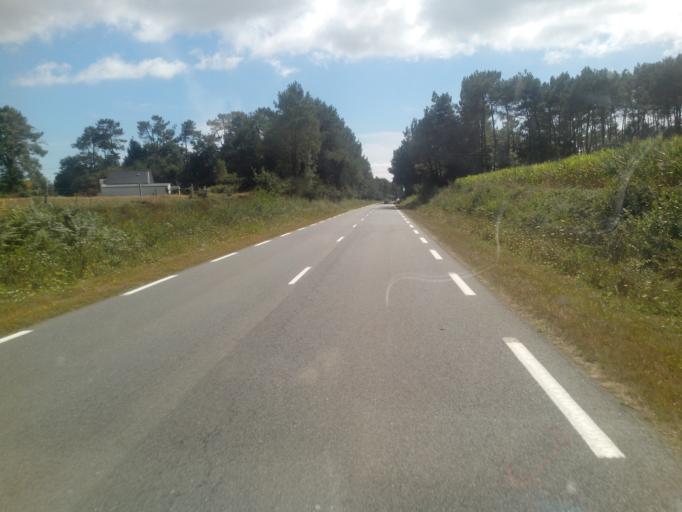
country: FR
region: Brittany
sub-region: Departement du Morbihan
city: Peaule
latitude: 47.5819
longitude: -2.3778
